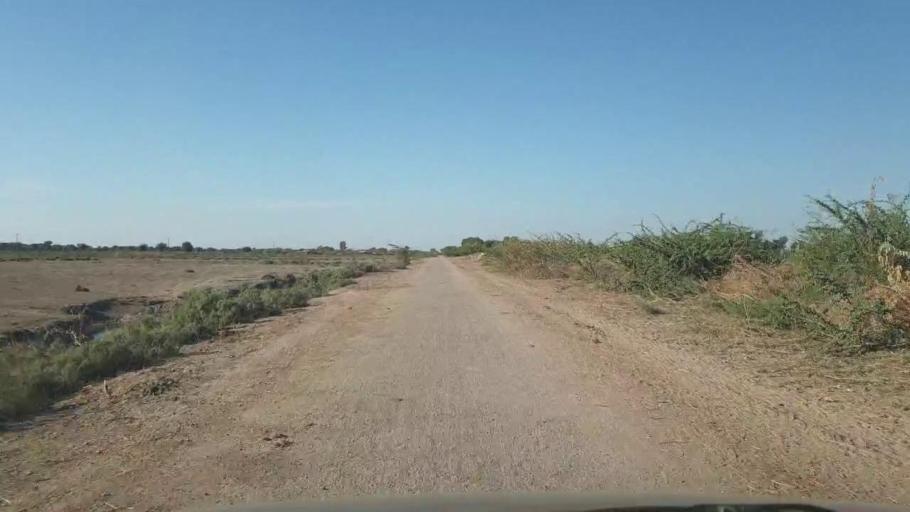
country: PK
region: Sindh
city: Dhoro Naro
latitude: 25.4244
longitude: 69.5563
